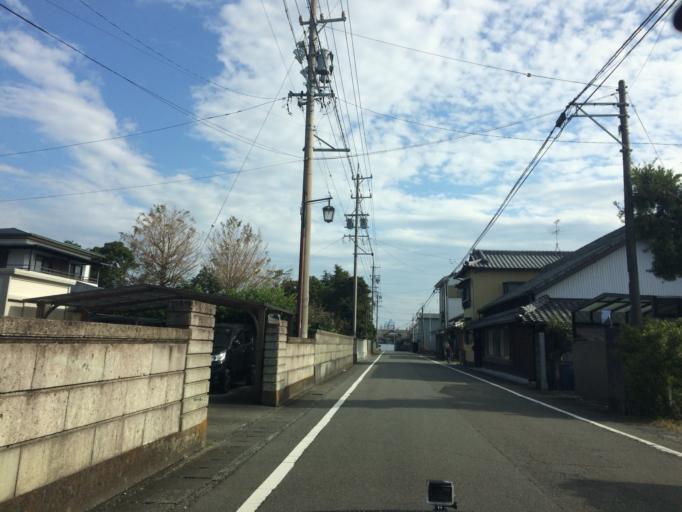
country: JP
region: Shizuoka
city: Sagara
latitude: 34.7560
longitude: 138.2410
